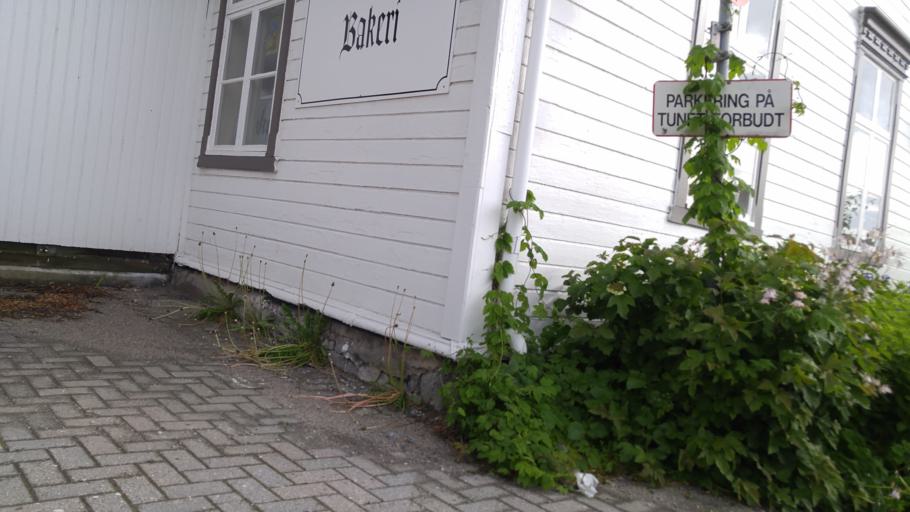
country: NO
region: Nord-Trondelag
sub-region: Vikna
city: Rorvik
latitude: 64.8618
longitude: 11.2336
